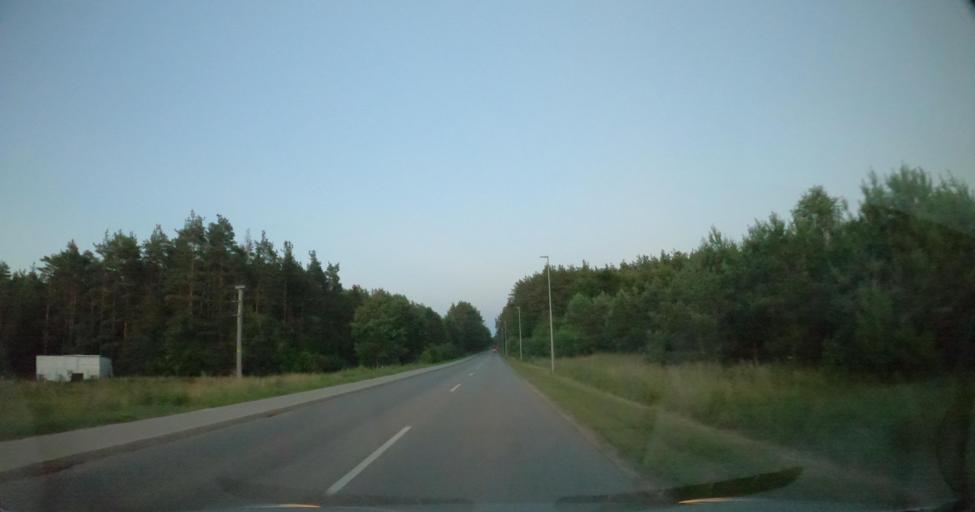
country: PL
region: Pomeranian Voivodeship
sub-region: Powiat wejherowski
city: Szemud
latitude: 54.4832
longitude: 18.2437
